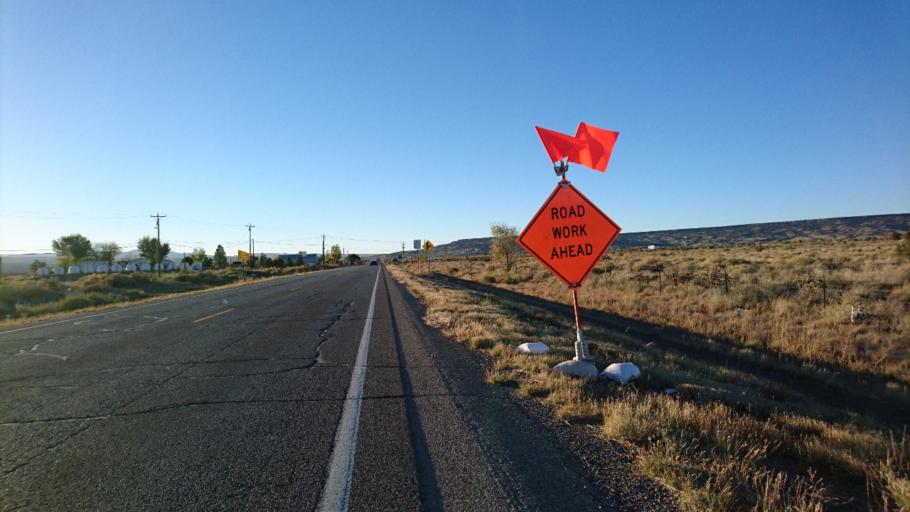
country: US
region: New Mexico
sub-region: Cibola County
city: Grants
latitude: 35.1337
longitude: -107.8165
